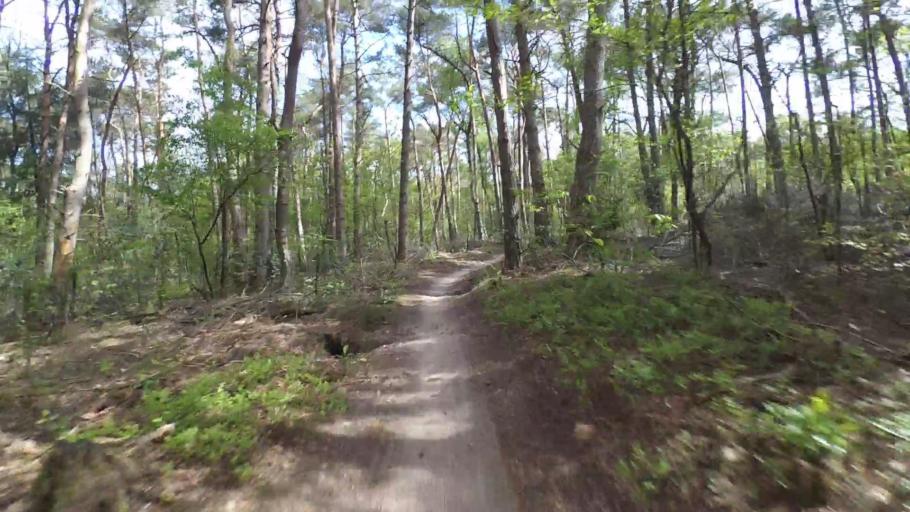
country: NL
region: Utrecht
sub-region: Gemeente Utrechtse Heuvelrug
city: Driebergen-Rijsenburg
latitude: 52.0792
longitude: 5.2771
